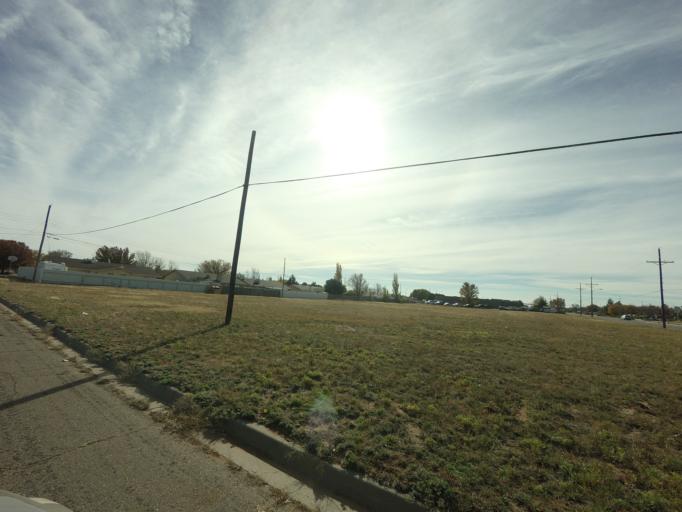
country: US
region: New Mexico
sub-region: Curry County
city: Clovis
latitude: 34.4231
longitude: -103.2314
